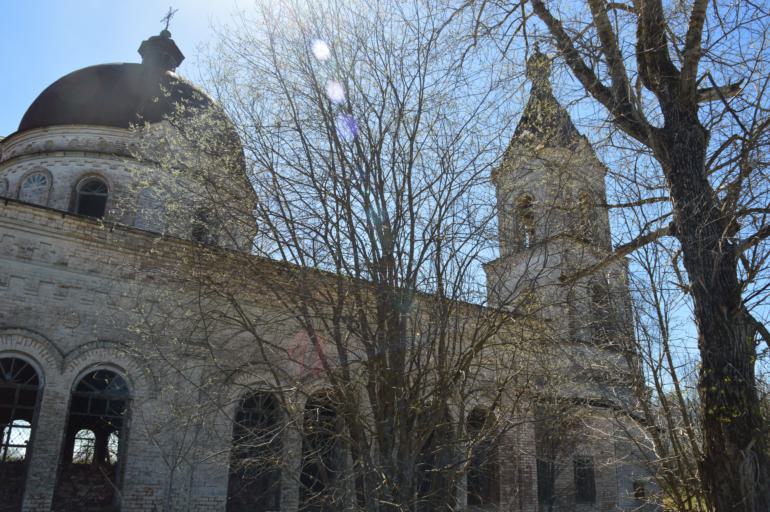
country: RU
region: Kirov
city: Murygino
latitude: 58.9251
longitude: 49.6676
